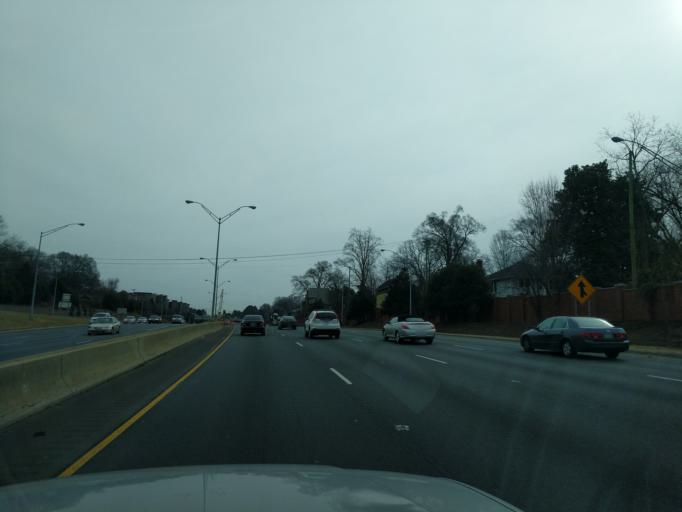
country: US
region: North Carolina
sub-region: Mecklenburg County
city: Charlotte
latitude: 35.2190
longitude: -80.8235
